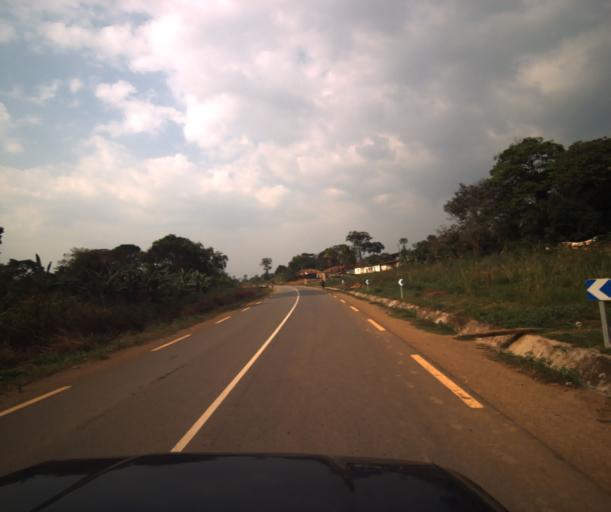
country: CM
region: Centre
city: Mbankomo
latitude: 3.7173
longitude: 11.3815
